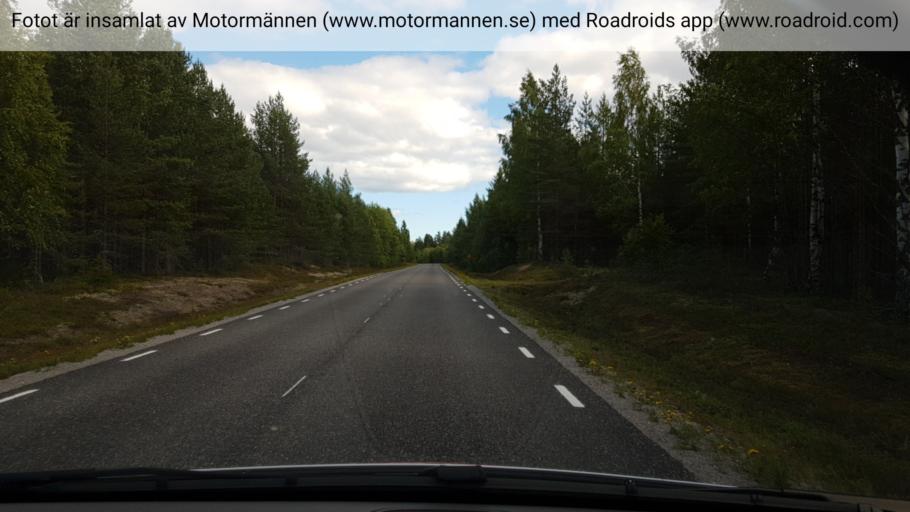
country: SE
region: Vaesterbotten
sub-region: Umea Kommun
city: Hoernefors
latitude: 63.6854
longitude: 19.8832
